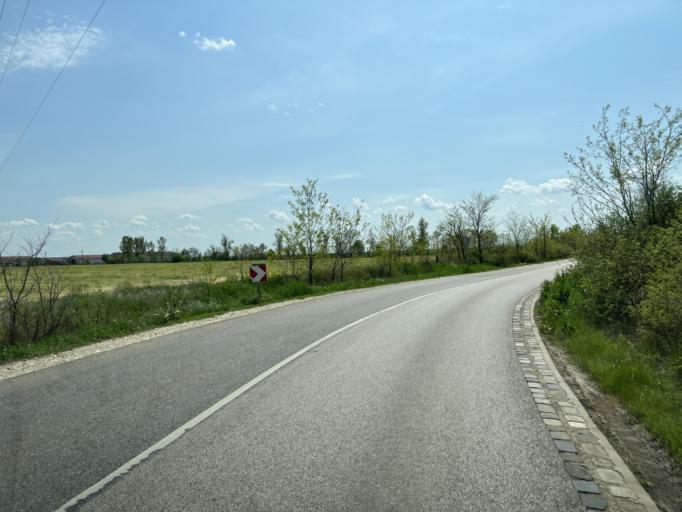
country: HU
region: Pest
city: Tapioszentmarton
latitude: 47.3064
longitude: 19.7612
